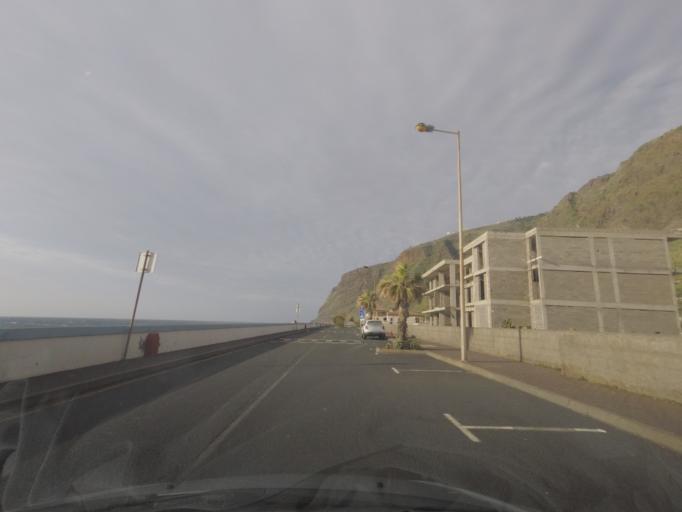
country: PT
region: Madeira
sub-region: Calheta
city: Faja da Ovelha
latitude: 32.7582
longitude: -17.2309
